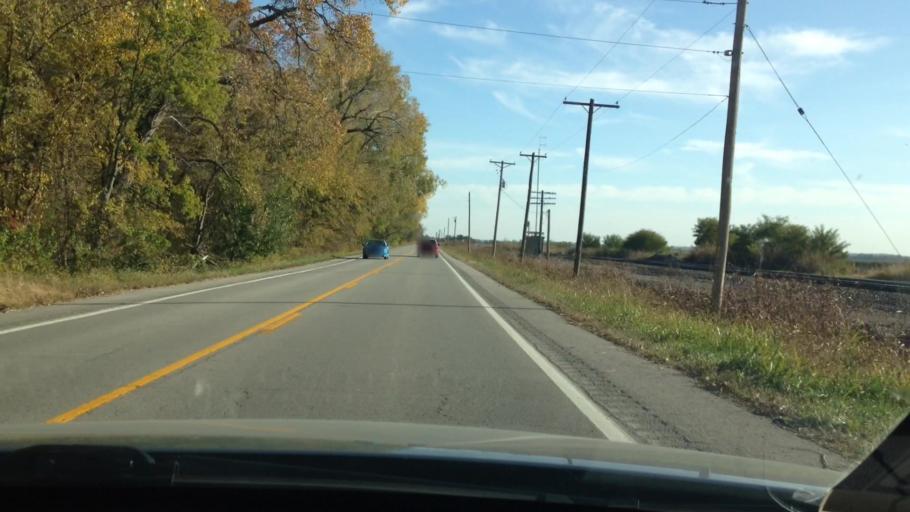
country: US
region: Kansas
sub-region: Leavenworth County
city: Lansing
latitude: 39.2985
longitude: -94.8451
